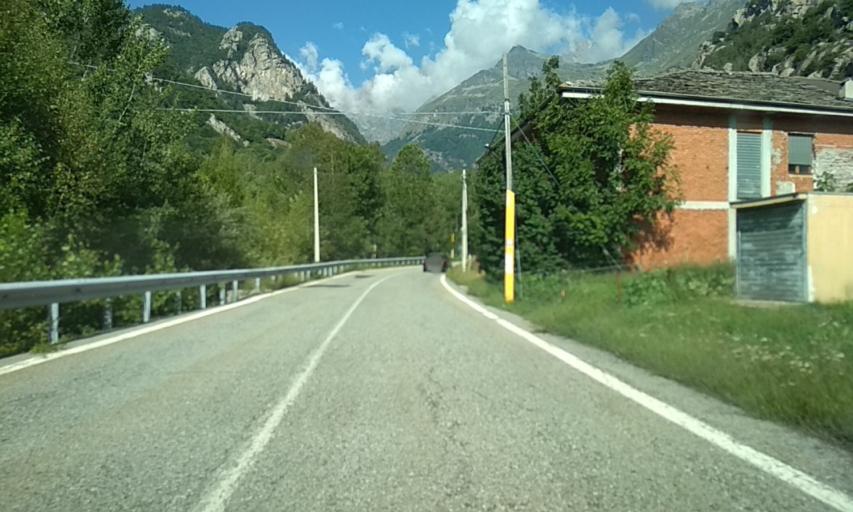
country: IT
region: Piedmont
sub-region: Provincia di Torino
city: Noasca
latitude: 45.4437
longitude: 7.3354
